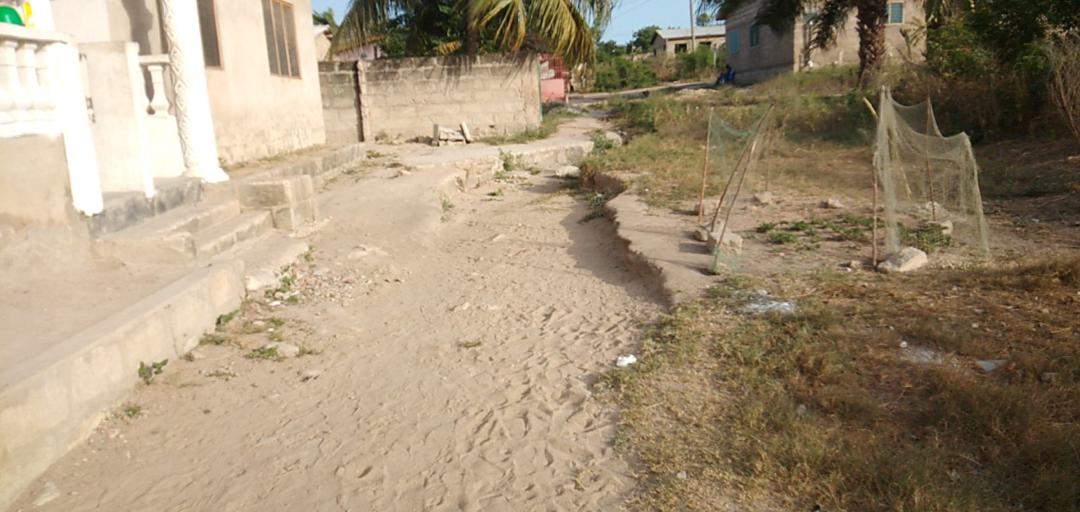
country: GH
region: Central
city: Winneba
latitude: 5.3579
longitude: -0.6161
